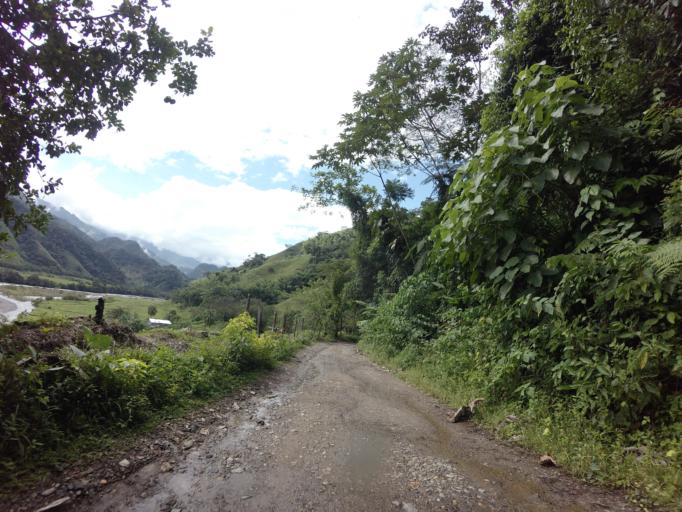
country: CO
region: Antioquia
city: Narino
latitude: 5.5367
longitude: -75.1356
